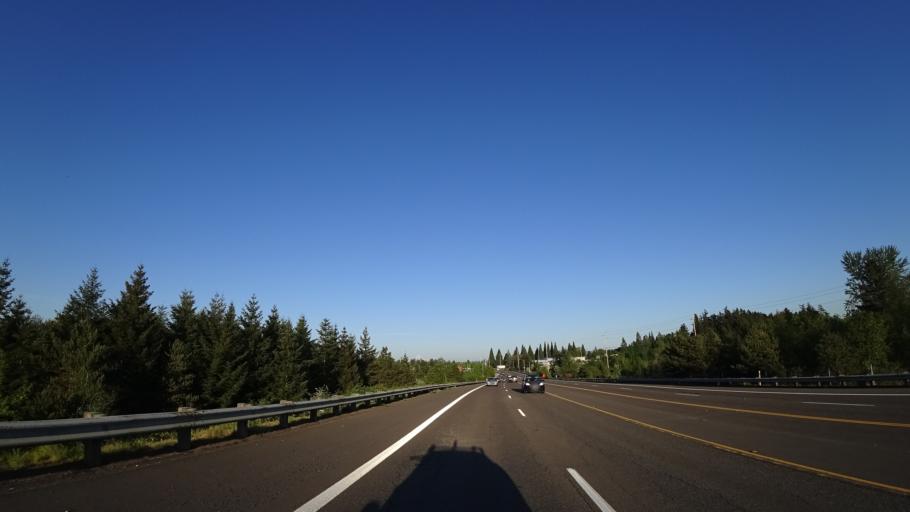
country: US
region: Oregon
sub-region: Washington County
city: Aloha
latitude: 45.4914
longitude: -122.8365
